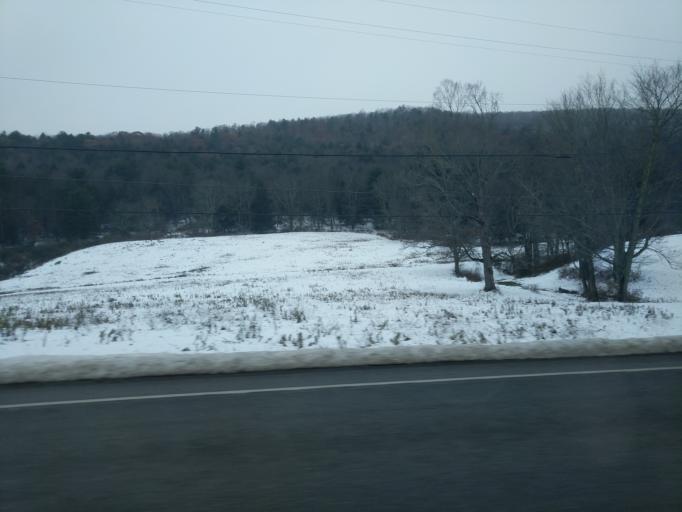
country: US
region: Pennsylvania
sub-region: Tioga County
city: Wellsboro
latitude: 41.8017
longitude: -77.3009
